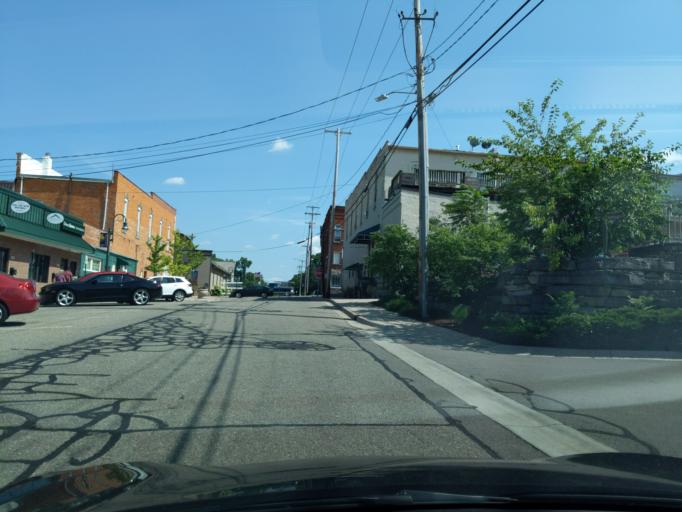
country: US
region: Michigan
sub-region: Eaton County
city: Grand Ledge
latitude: 42.7545
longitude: -84.7458
